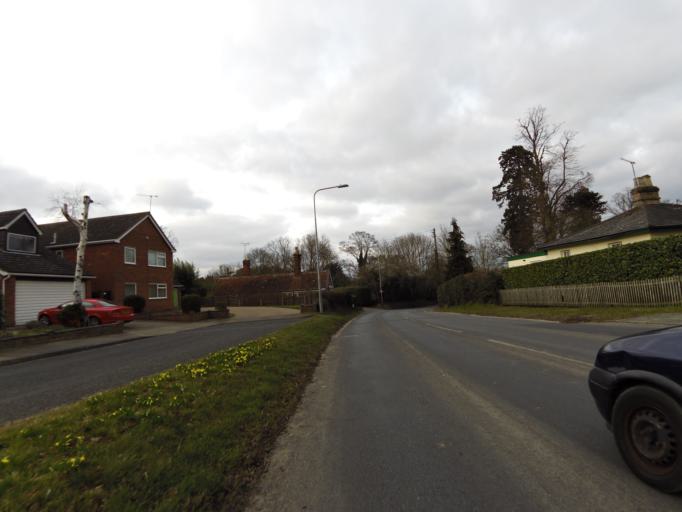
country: GB
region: England
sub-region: Suffolk
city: Ipswich
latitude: 52.0858
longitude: 1.1495
